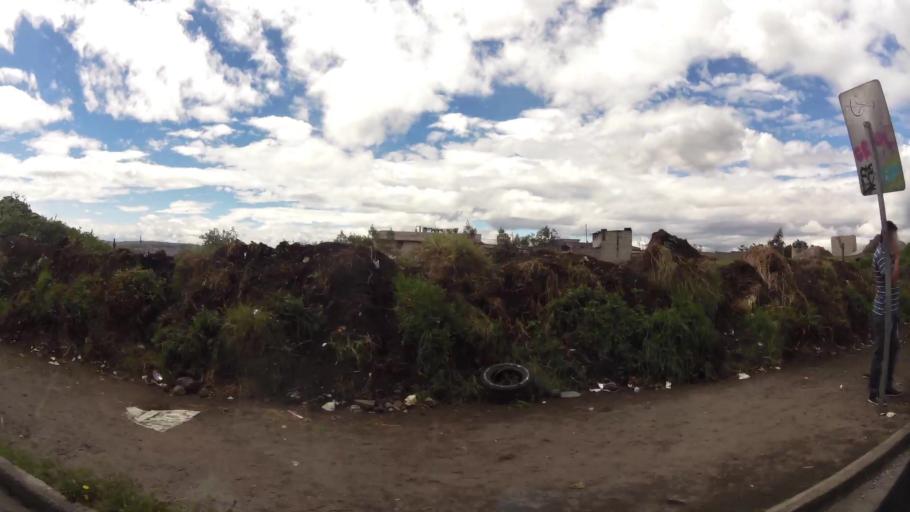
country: EC
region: Pichincha
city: Sangolqui
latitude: -0.3344
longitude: -78.5557
